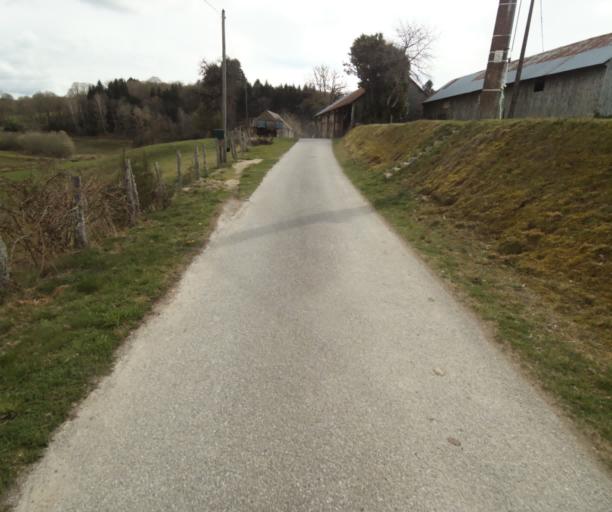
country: FR
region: Limousin
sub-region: Departement de la Correze
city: Correze
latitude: 45.3866
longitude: 1.8961
